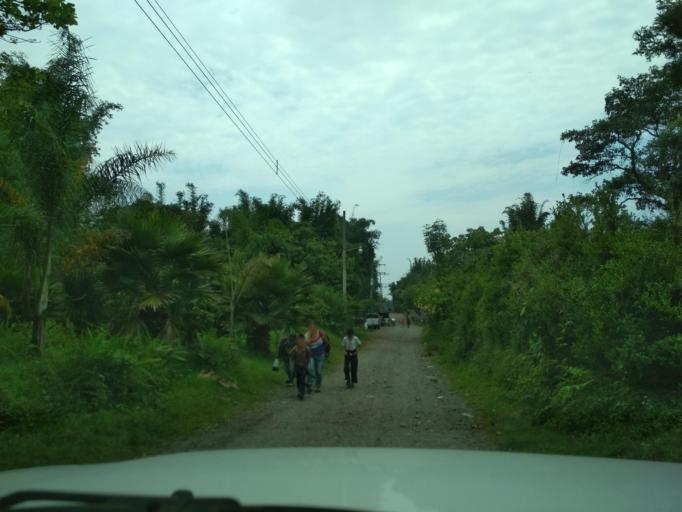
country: MX
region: Veracruz
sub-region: La Perla
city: La Perla
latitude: 18.9248
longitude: -97.1273
